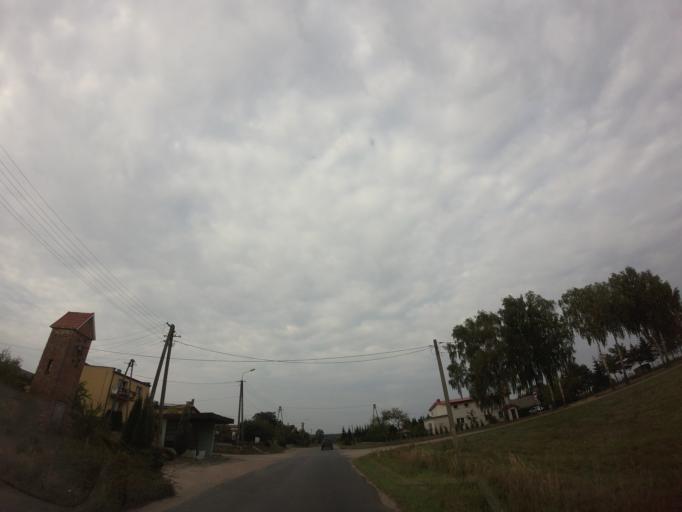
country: PL
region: West Pomeranian Voivodeship
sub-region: Powiat drawski
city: Drawsko Pomorskie
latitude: 53.4937
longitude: 15.7807
